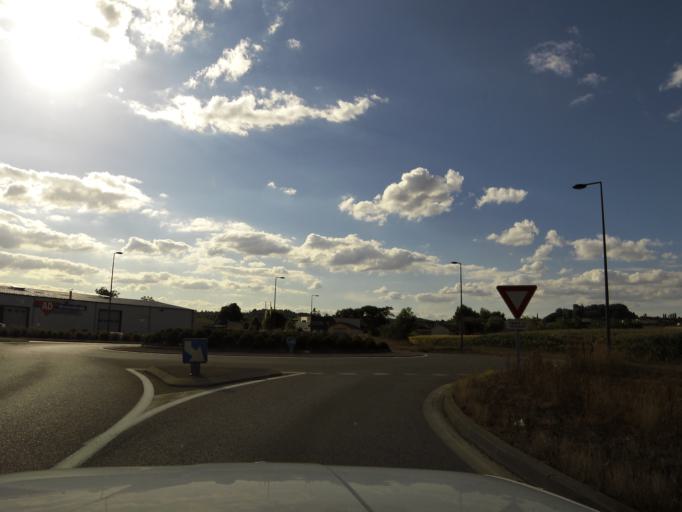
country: FR
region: Rhone-Alpes
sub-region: Departement de l'Ain
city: Meximieux
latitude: 45.8963
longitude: 5.1997
